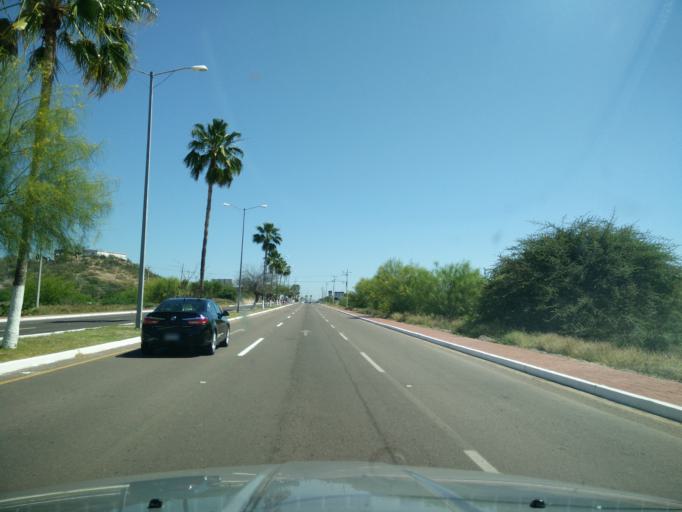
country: MX
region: Sonora
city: Heroica Guaymas
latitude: 27.9541
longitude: -111.0488
